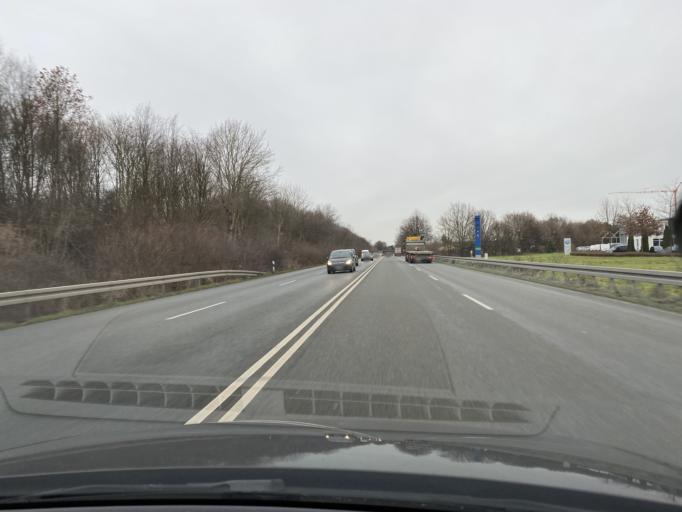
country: DE
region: North Rhine-Westphalia
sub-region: Regierungsbezirk Arnsberg
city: Lippstadt
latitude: 51.6540
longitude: 8.3495
